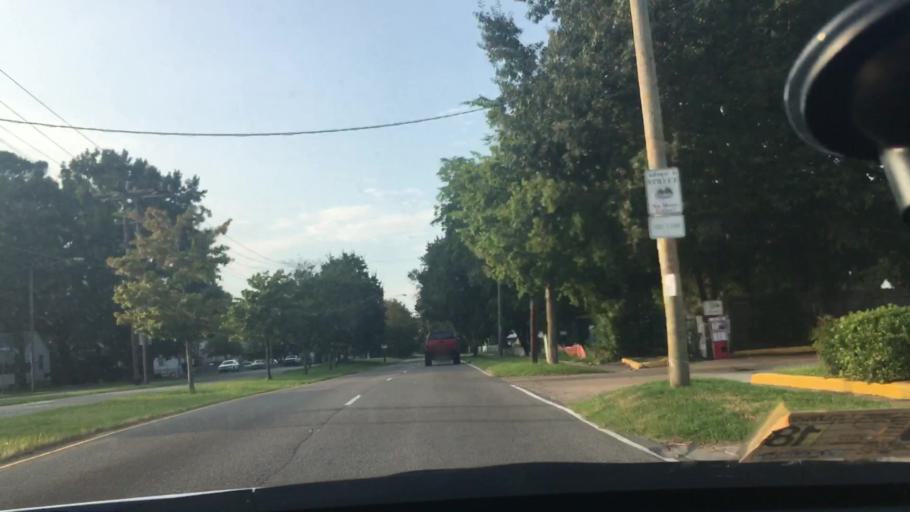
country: US
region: Virginia
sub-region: City of Norfolk
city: Norfolk
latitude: 36.9340
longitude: -76.2443
